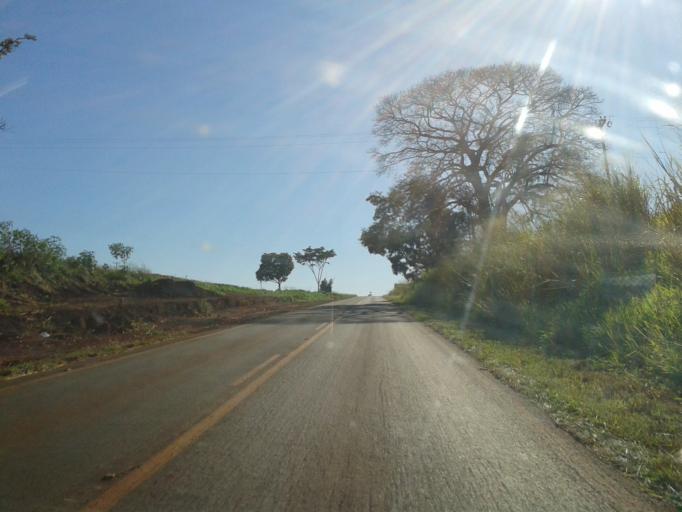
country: BR
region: Minas Gerais
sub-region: Capinopolis
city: Capinopolis
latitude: -18.6707
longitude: -49.5616
